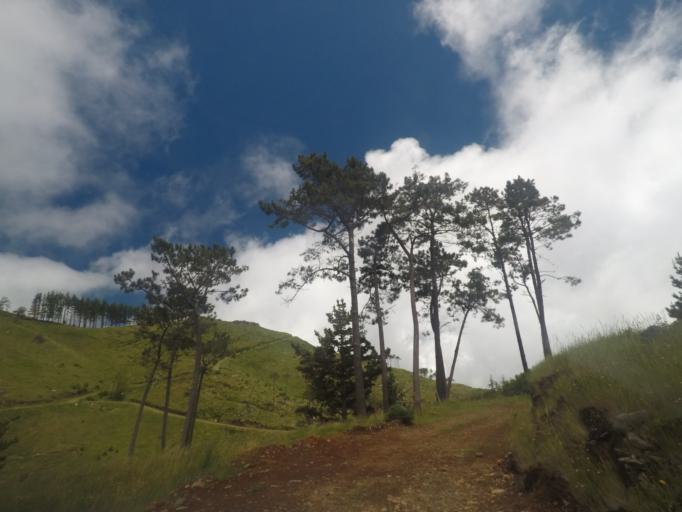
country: PT
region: Madeira
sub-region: Funchal
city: Nossa Senhora do Monte
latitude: 32.7035
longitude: -16.9043
